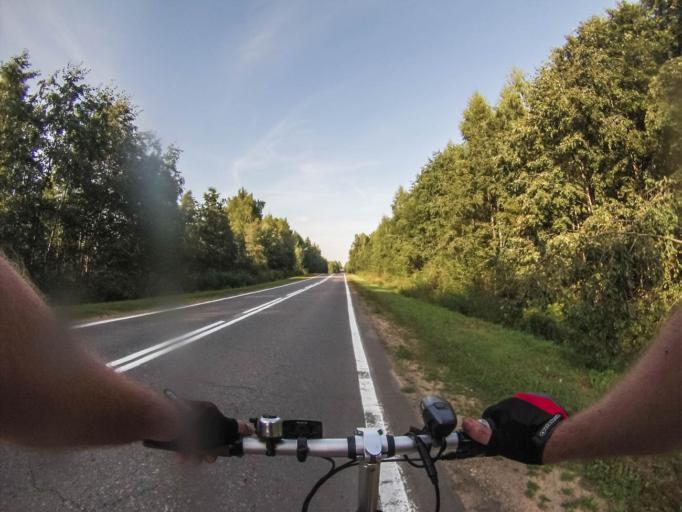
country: RU
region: Jaroslavl
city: Myshkin
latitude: 57.7203
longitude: 38.4117
